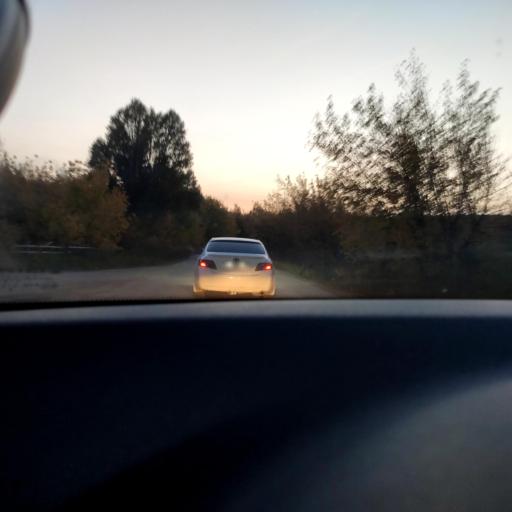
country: RU
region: Samara
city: Novosemeykino
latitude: 53.3554
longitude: 50.3457
